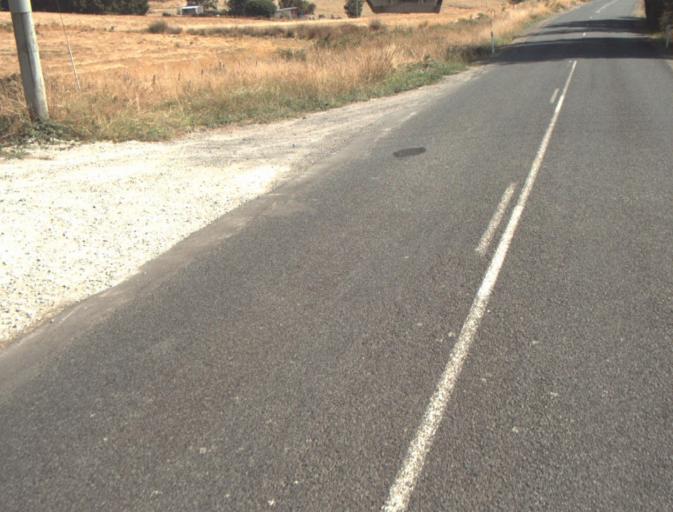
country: AU
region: Tasmania
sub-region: Launceston
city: Mayfield
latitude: -41.1903
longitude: 147.2215
